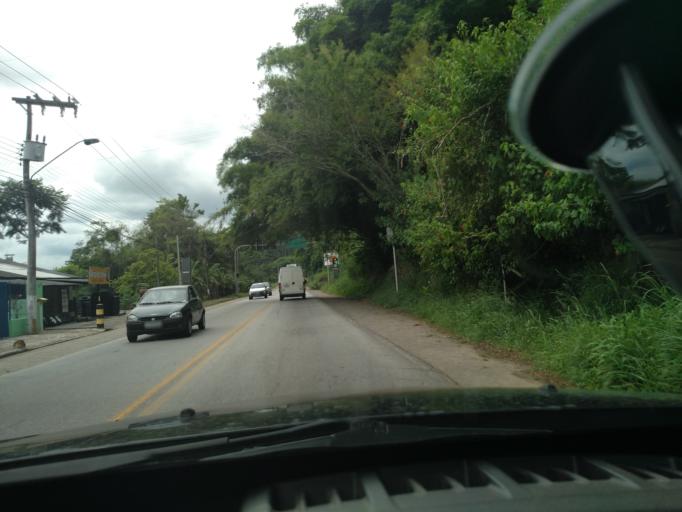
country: BR
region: Santa Catarina
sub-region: Blumenau
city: Blumenau
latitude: -26.9092
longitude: -49.0283
